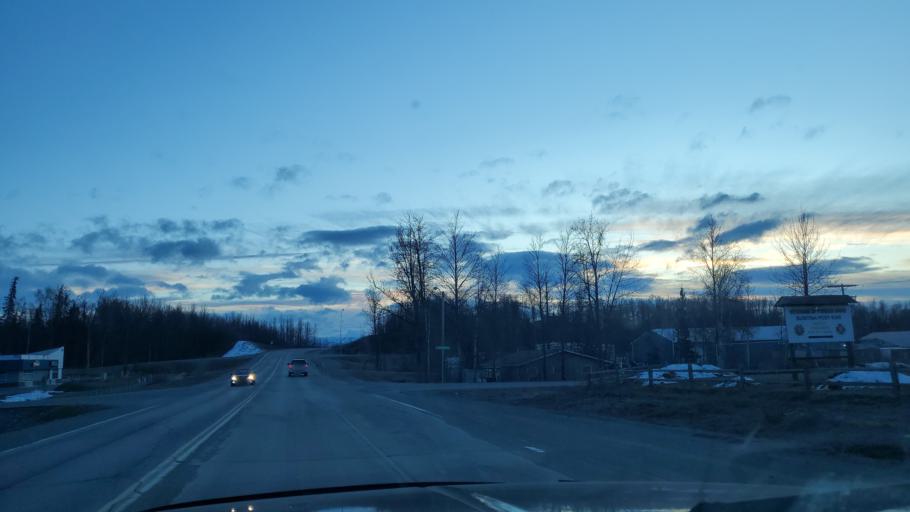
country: US
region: Alaska
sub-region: Matanuska-Susitna Borough
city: Wasilla
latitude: 61.5774
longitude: -149.4415
